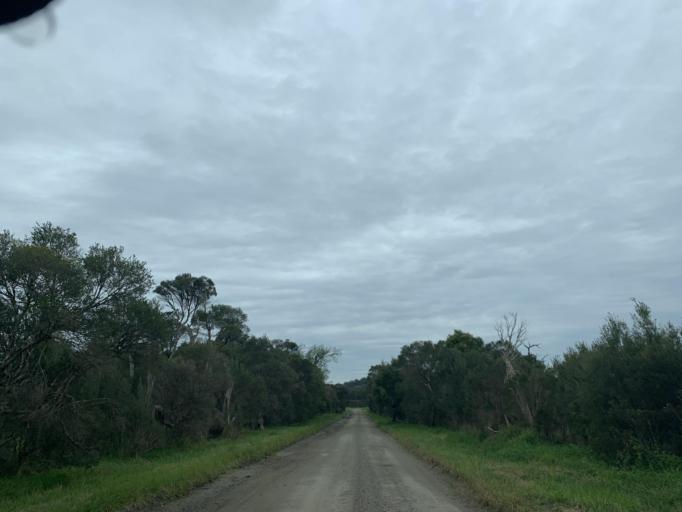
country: AU
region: Victoria
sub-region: Cardinia
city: Garfield
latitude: -38.0939
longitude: 145.6412
